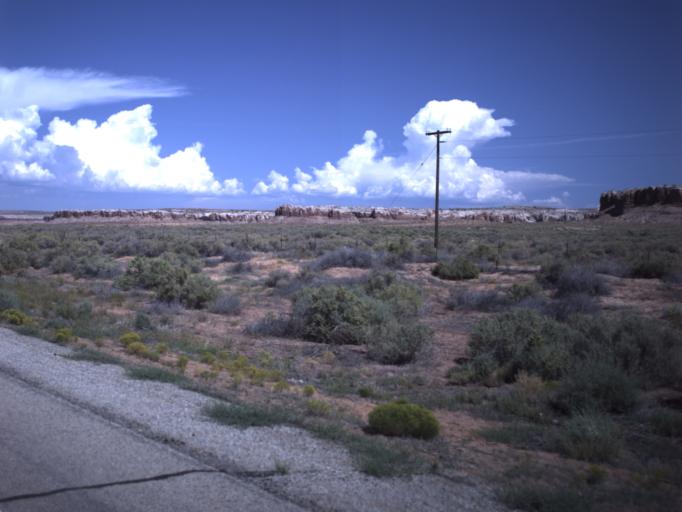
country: US
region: Utah
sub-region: San Juan County
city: Blanding
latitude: 37.1828
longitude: -109.5897
